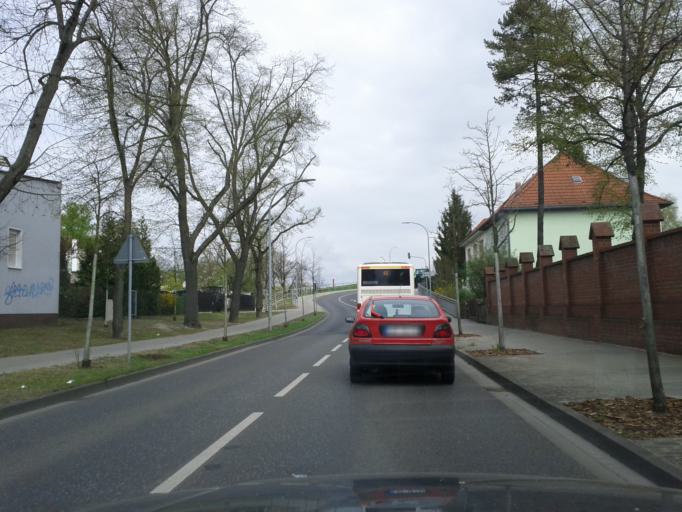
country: DE
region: Brandenburg
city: Furstenwalde
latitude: 52.3633
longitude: 14.0672
